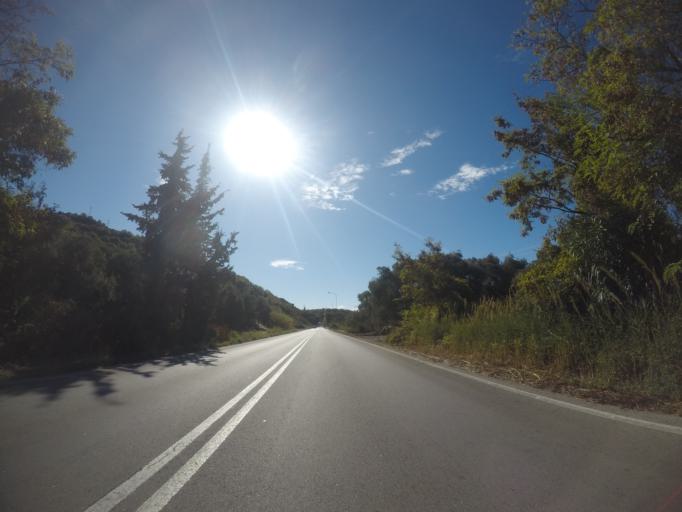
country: GR
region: Epirus
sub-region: Nomos Prevezis
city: Kanalaki
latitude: 39.1688
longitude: 20.5583
